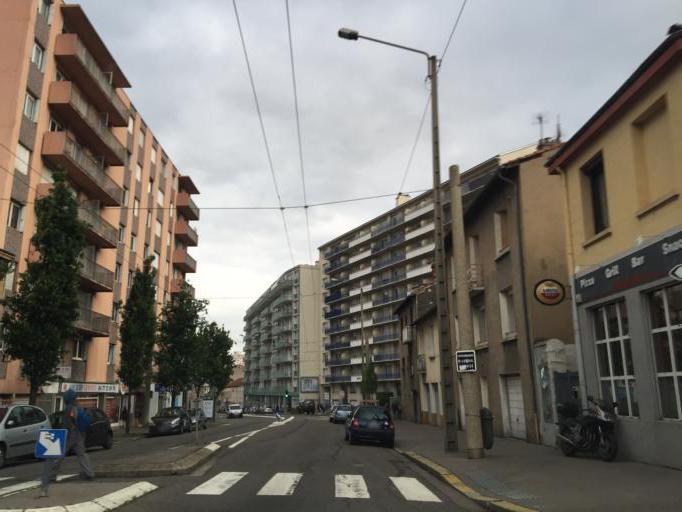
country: FR
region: Rhone-Alpes
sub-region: Departement de la Loire
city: Saint-Etienne
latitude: 45.4190
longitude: 4.3996
